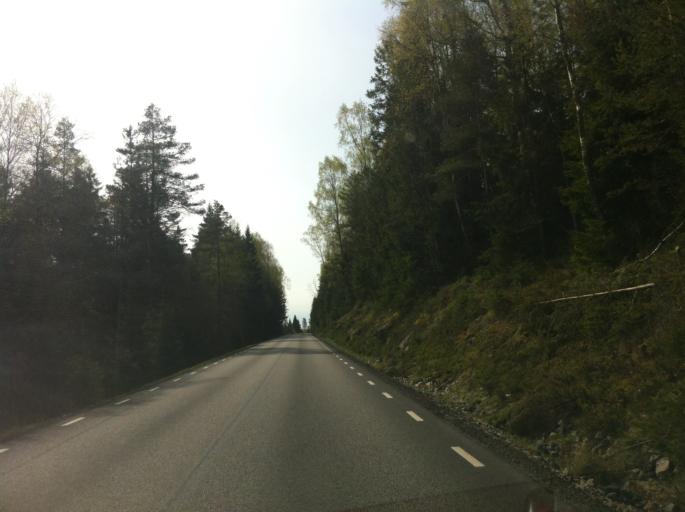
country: SE
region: Vaestra Goetaland
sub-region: Marks Kommun
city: Fritsla
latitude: 57.3582
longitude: 12.8666
